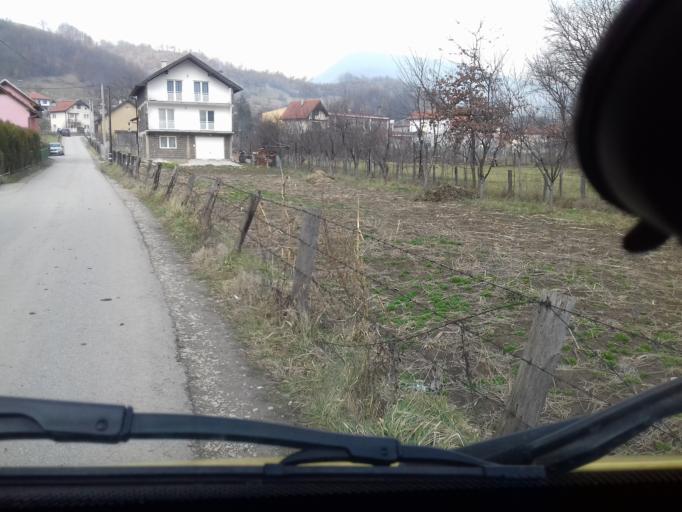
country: BA
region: Federation of Bosnia and Herzegovina
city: Kakanj
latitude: 44.1323
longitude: 18.0666
